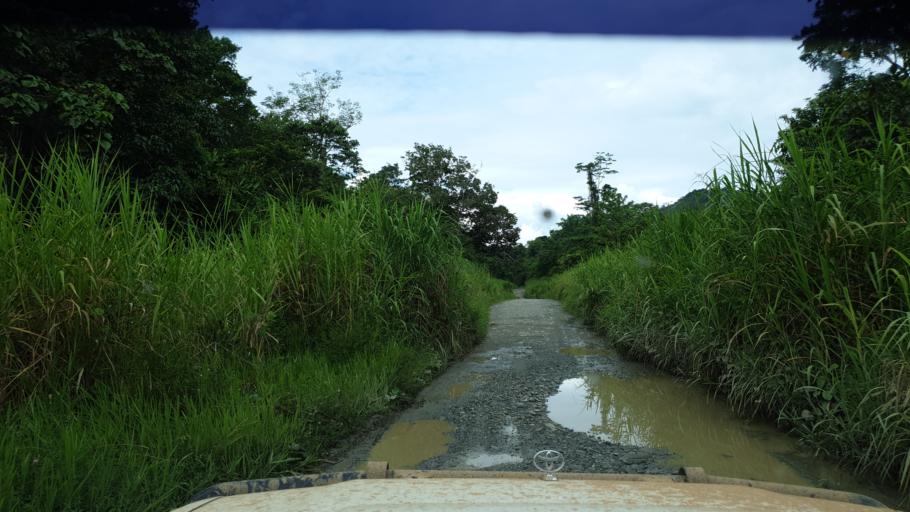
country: PG
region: Northern Province
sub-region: Sohe
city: Kokoda
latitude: -8.9165
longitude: 147.8577
